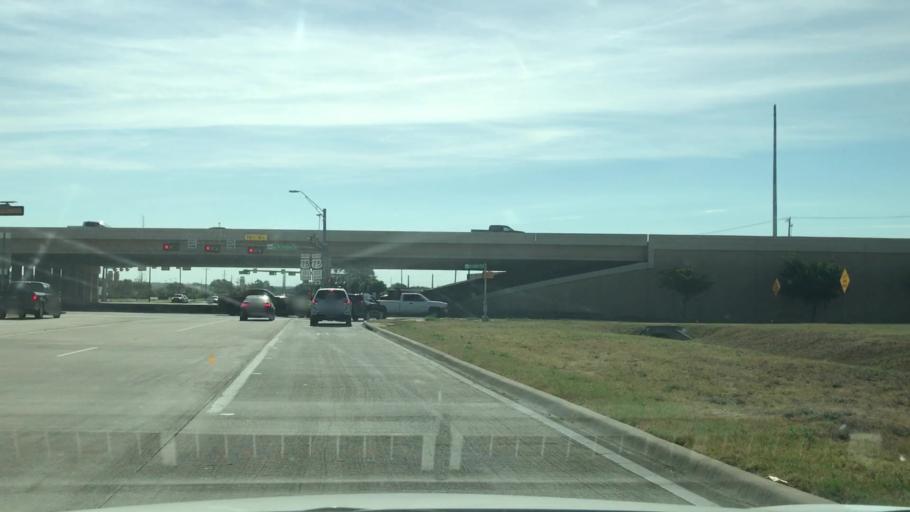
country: US
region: Texas
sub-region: Collin County
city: McKinney
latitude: 33.2291
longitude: -96.6342
